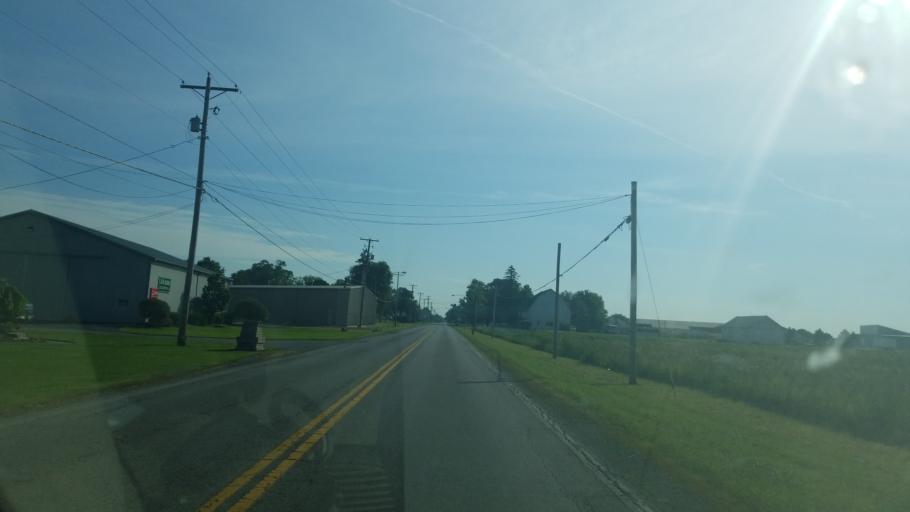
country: US
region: Ohio
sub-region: Hancock County
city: Findlay
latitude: 41.0132
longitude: -83.6830
